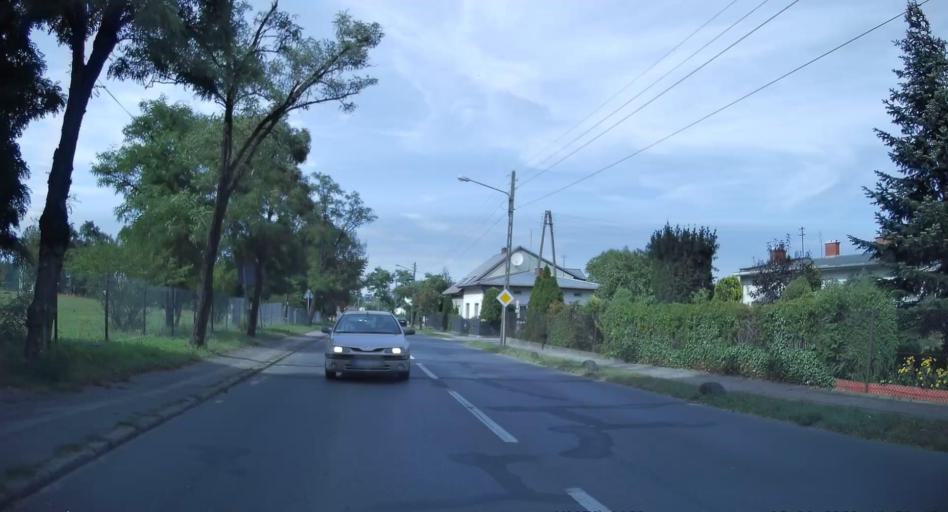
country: PL
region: Lodz Voivodeship
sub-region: Powiat tomaszowski
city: Tomaszow Mazowiecki
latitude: 51.5309
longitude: 19.9968
